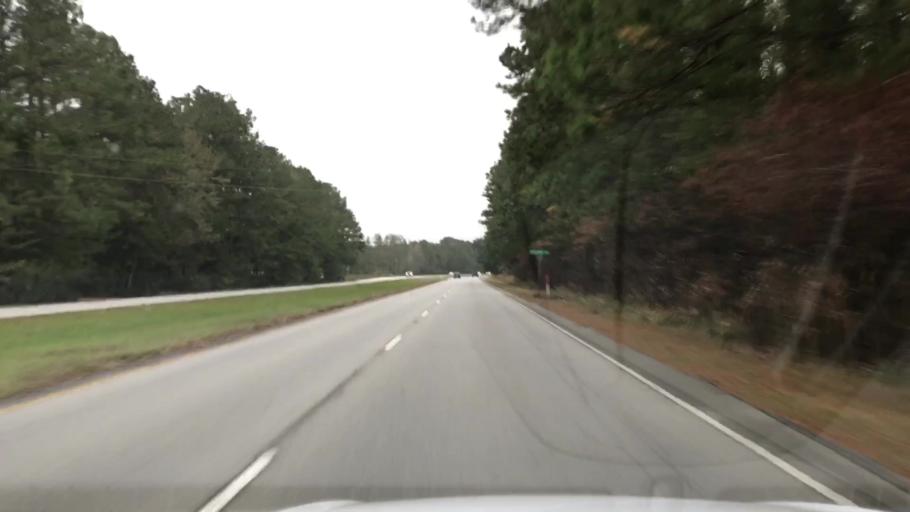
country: US
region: South Carolina
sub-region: Charleston County
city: Awendaw
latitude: 32.9988
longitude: -79.6441
